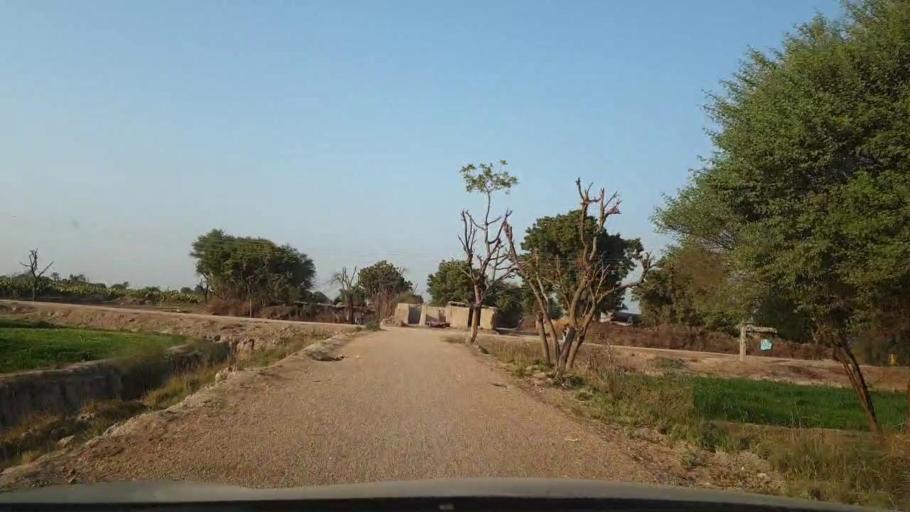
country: PK
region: Sindh
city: Tando Allahyar
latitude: 25.5703
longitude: 68.7932
